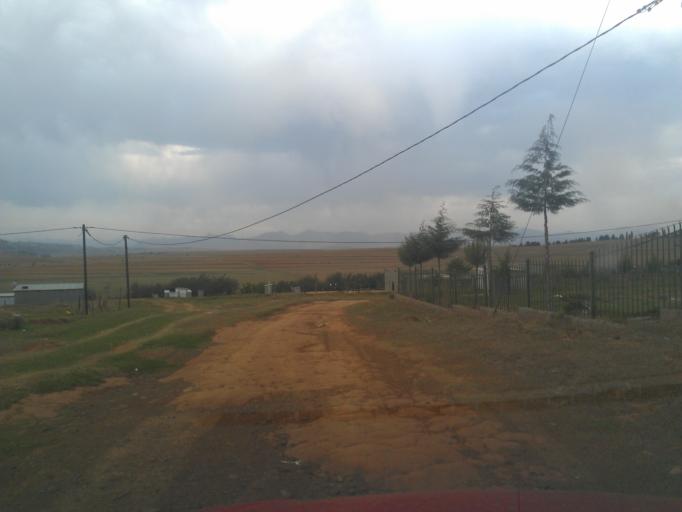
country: LS
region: Berea
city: Teyateyaneng
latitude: -29.1272
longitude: 27.7634
